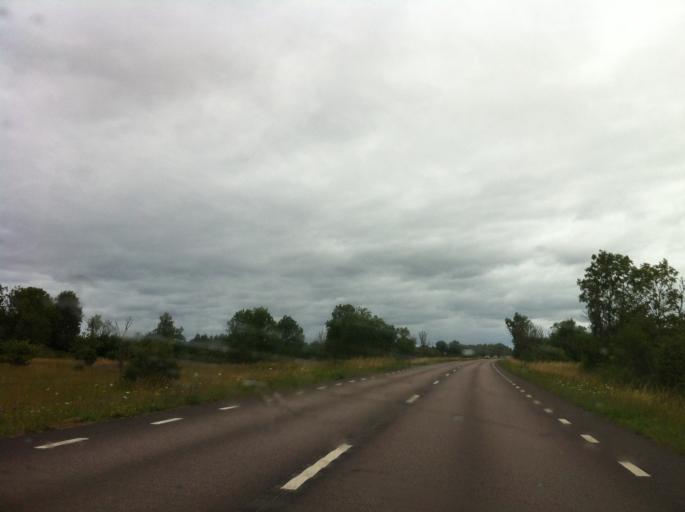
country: SE
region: Kalmar
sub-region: Borgholms Kommun
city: Borgholm
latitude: 57.0924
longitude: 16.9255
